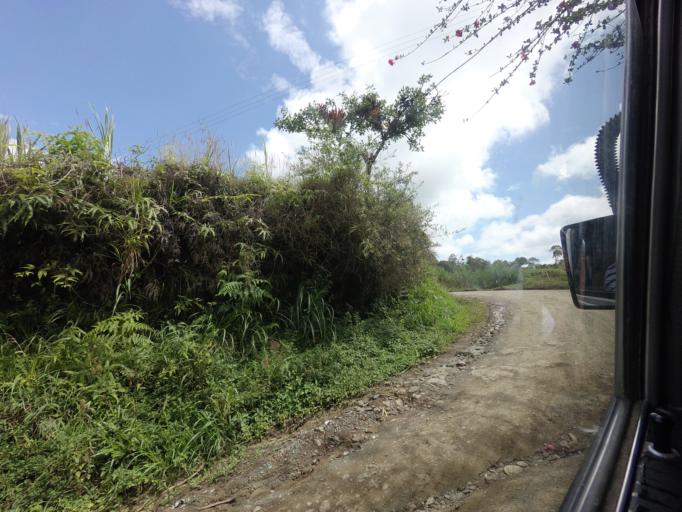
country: CO
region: Huila
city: Isnos
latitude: 1.9436
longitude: -76.2745
